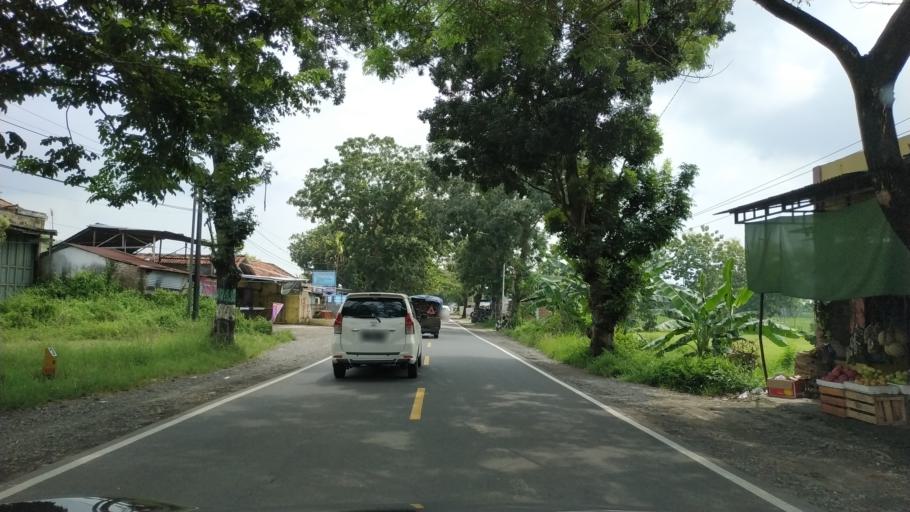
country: ID
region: Central Java
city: Slawi
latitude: -7.0124
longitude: 109.1416
